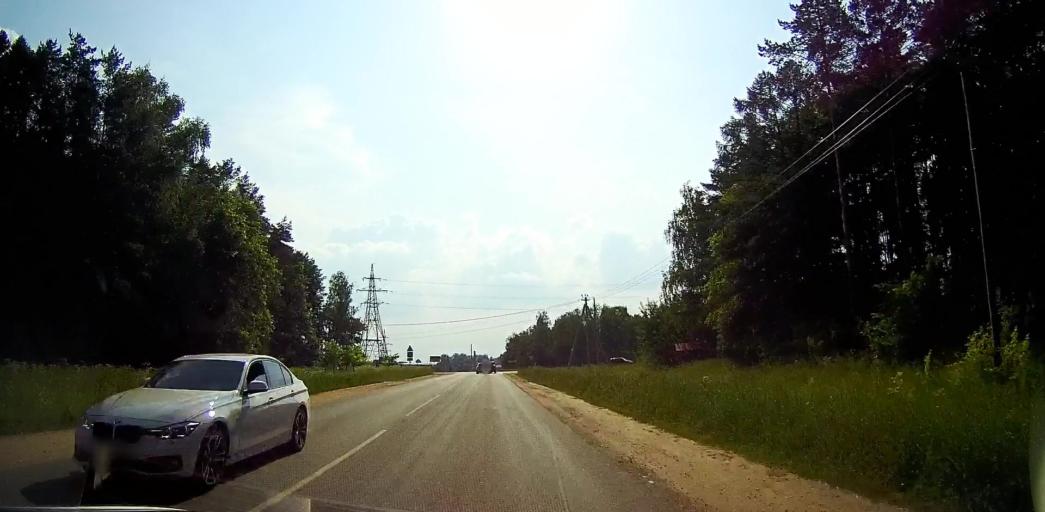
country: RU
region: Moskovskaya
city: Barybino
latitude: 55.2817
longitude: 37.9187
